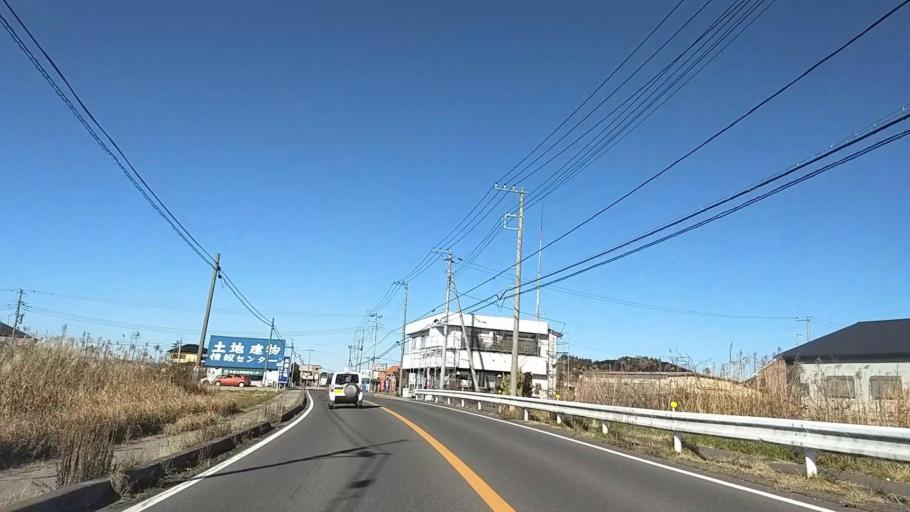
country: JP
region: Chiba
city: Ohara
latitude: 35.3057
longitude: 140.4010
